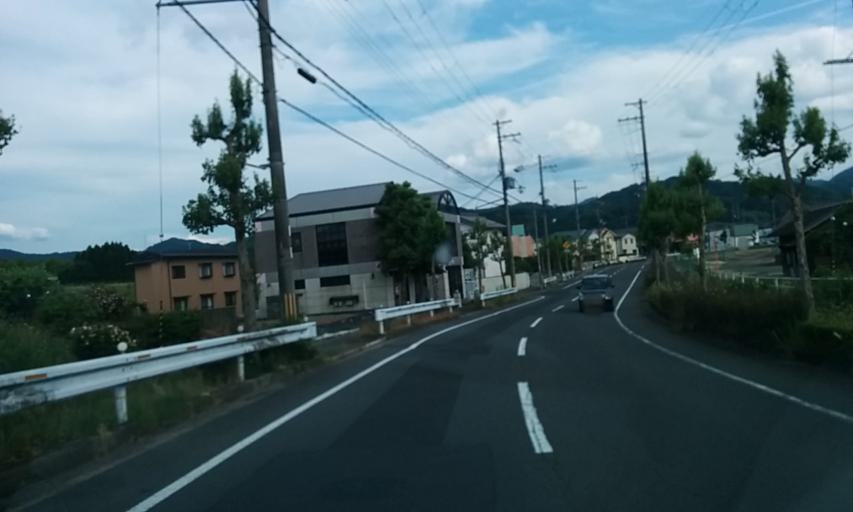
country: JP
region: Kyoto
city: Ayabe
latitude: 35.3074
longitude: 135.2611
